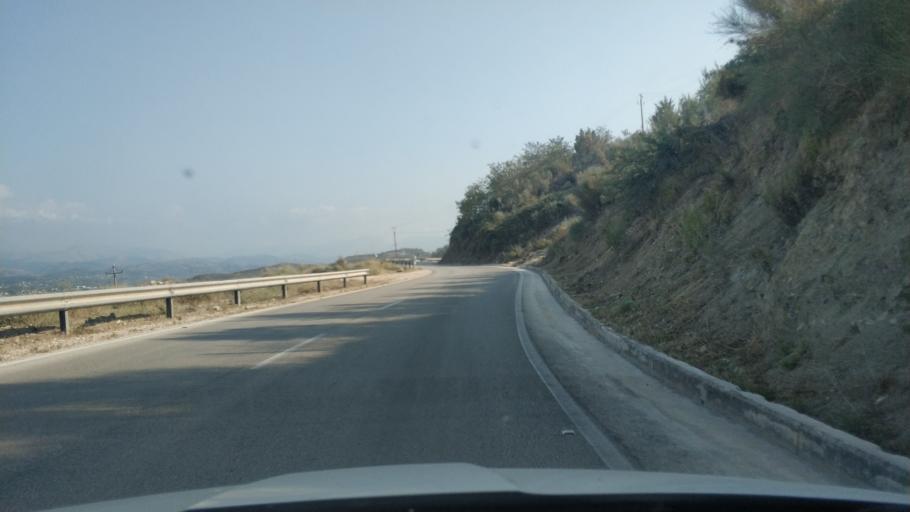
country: AL
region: Vlore
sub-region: Rrethi i Sarandes
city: Sarande
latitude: 39.8954
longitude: 20.0114
